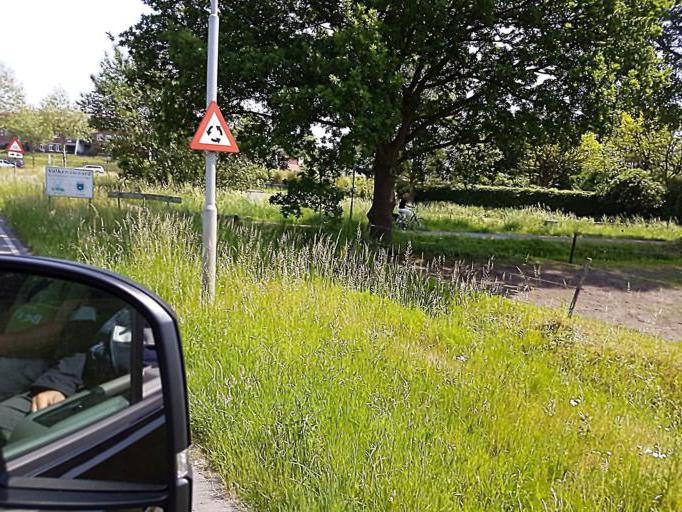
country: NL
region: North Brabant
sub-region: Gemeente Valkenswaard
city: Valkenswaard
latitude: 51.3427
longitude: 5.4484
